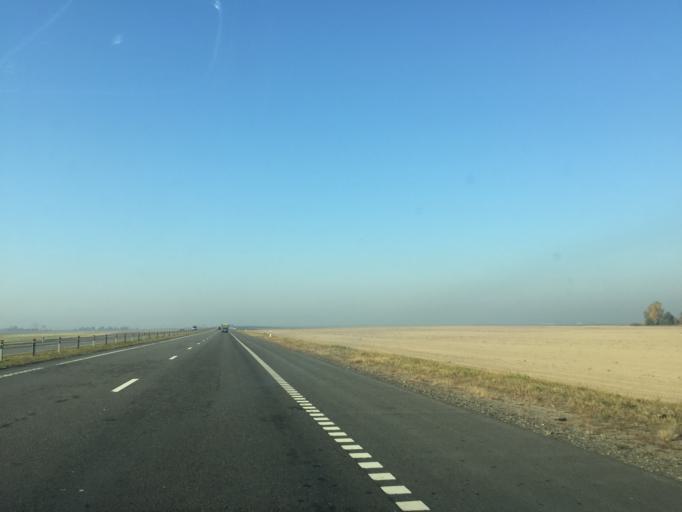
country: BY
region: Gomel
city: Kastsyukowka
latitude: 52.4939
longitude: 30.8454
